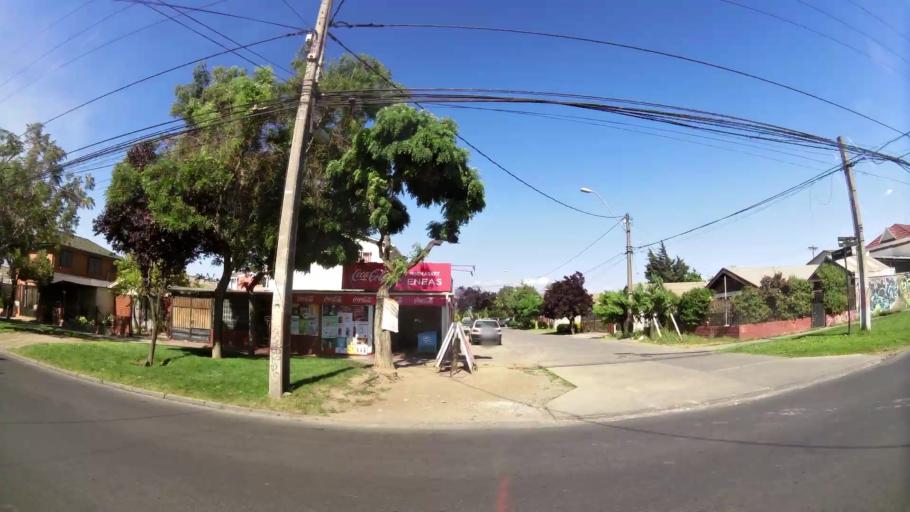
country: CL
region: Santiago Metropolitan
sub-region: Provincia de Santiago
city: Lo Prado
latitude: -33.5193
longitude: -70.7753
